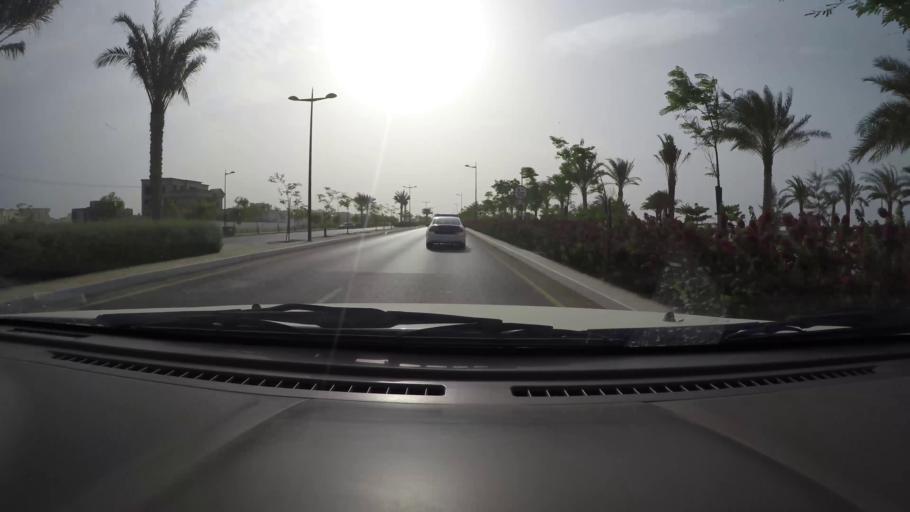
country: OM
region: Muhafazat Masqat
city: As Sib al Jadidah
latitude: 23.6971
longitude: 58.1503
